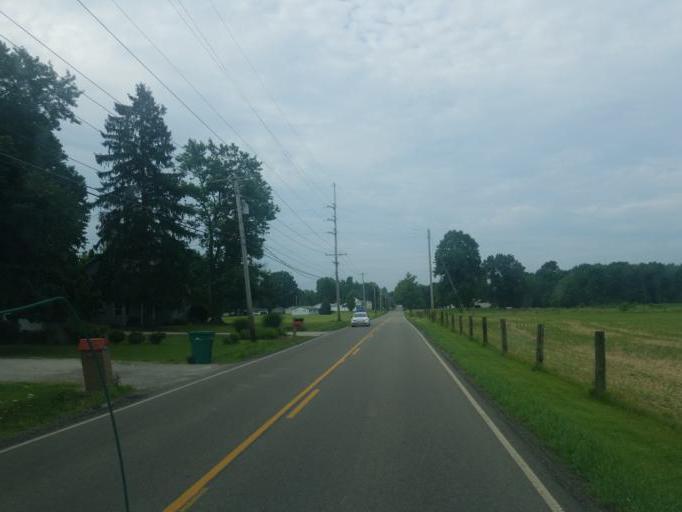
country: US
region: Ohio
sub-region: Wayne County
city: Apple Creek
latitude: 40.8035
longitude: -81.8442
